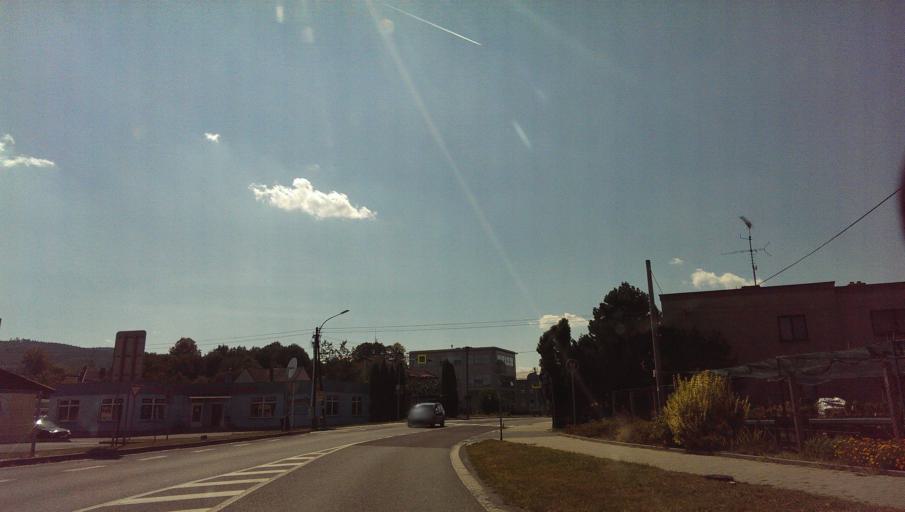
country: CZ
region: Zlin
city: Valasske Mezirici
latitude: 49.4670
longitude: 17.9525
